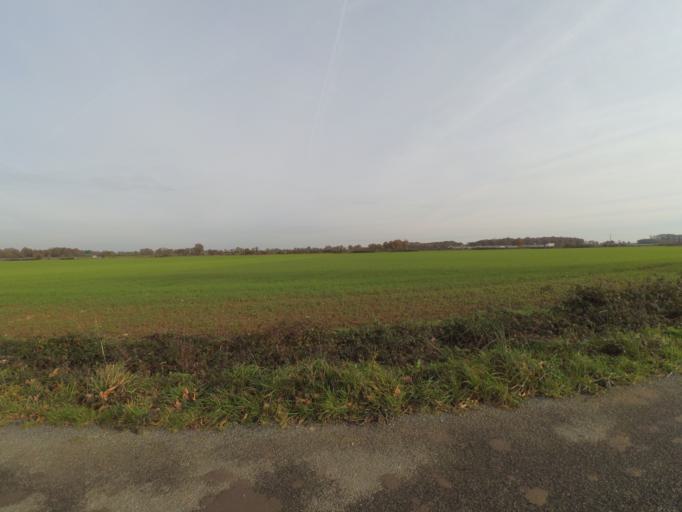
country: FR
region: Pays de la Loire
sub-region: Departement de la Loire-Atlantique
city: La Planche
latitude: 47.0125
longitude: -1.3935
